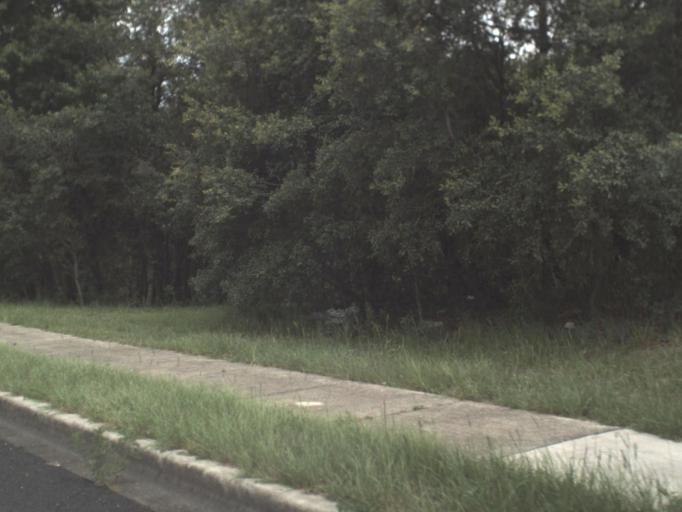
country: US
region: Florida
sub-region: Citrus County
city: Inverness Highlands North
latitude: 28.8540
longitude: -82.3891
